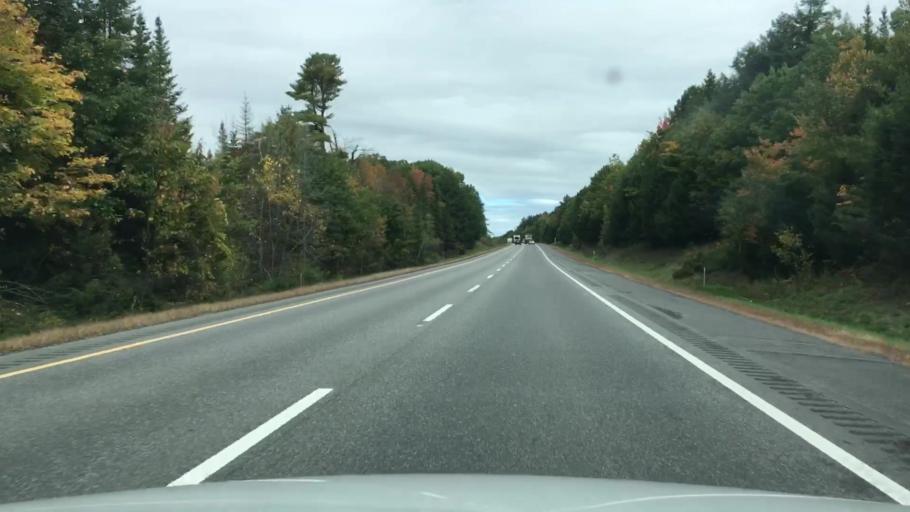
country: US
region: Maine
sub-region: Kennebec County
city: Sidney
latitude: 44.3923
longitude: -69.7577
